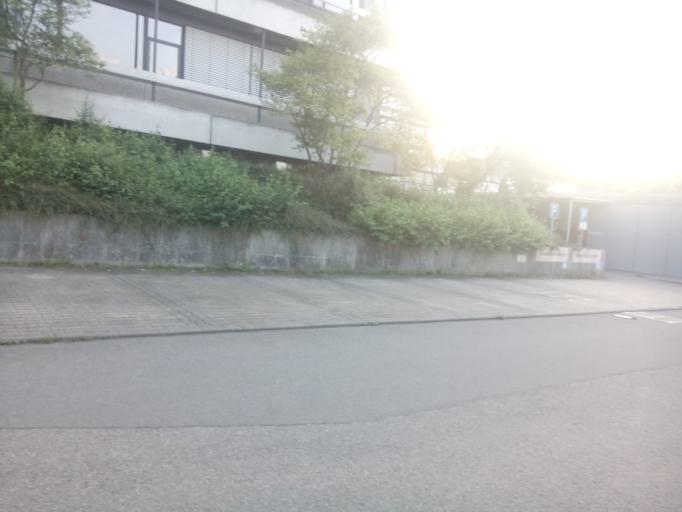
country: DE
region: Baden-Wuerttemberg
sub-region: Tuebingen Region
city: Tuebingen
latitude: 48.5379
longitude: 9.0375
